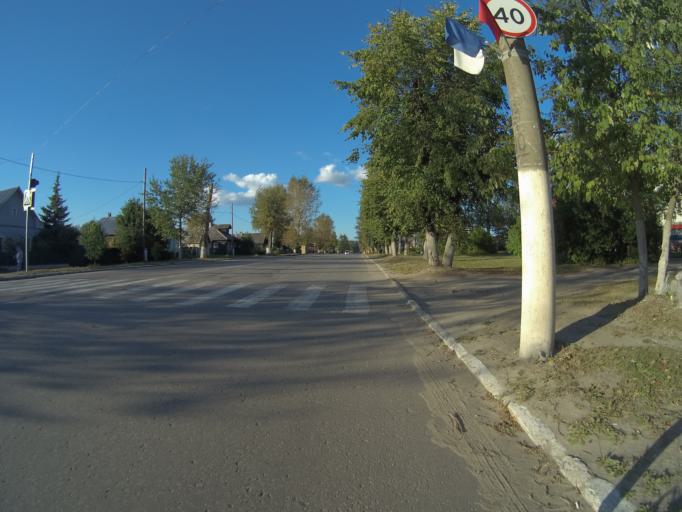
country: RU
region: Vladimir
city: Gus'-Khrustal'nyy
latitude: 55.6222
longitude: 40.6803
